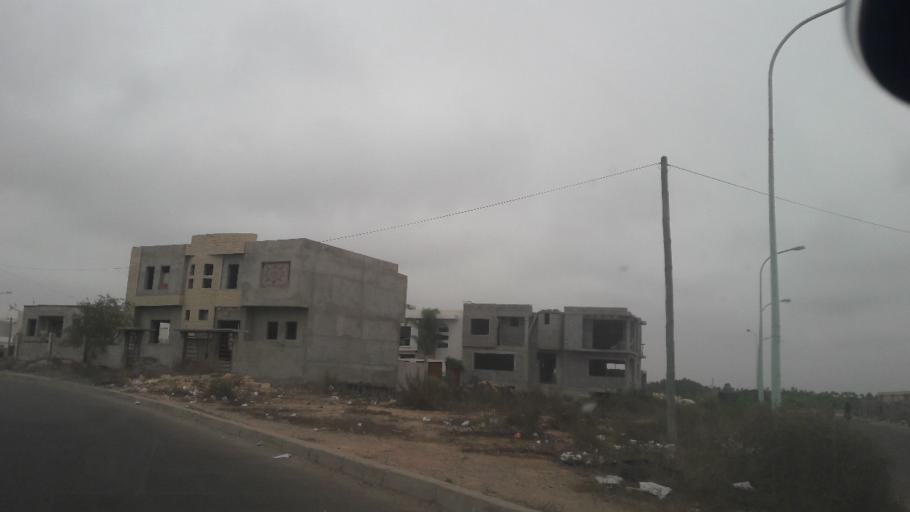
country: MA
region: Souss-Massa-Draa
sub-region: Agadir-Ida-ou-Tnan
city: Agadir
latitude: 30.3893
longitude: -9.5885
